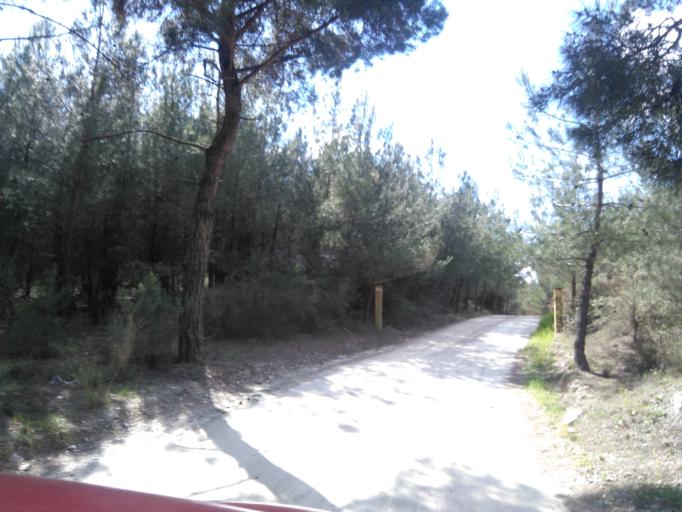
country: GR
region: Central Macedonia
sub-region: Nomos Thessalonikis
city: Pefka
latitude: 40.6412
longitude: 22.9992
